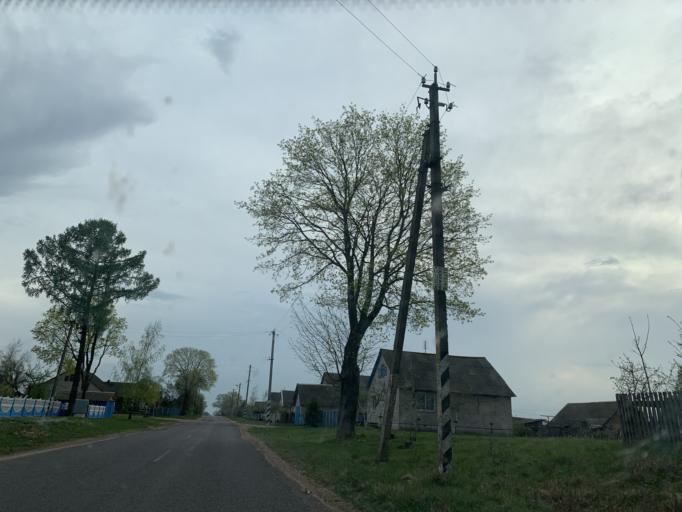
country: BY
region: Minsk
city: Kapyl'
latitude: 53.2853
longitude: 26.9842
